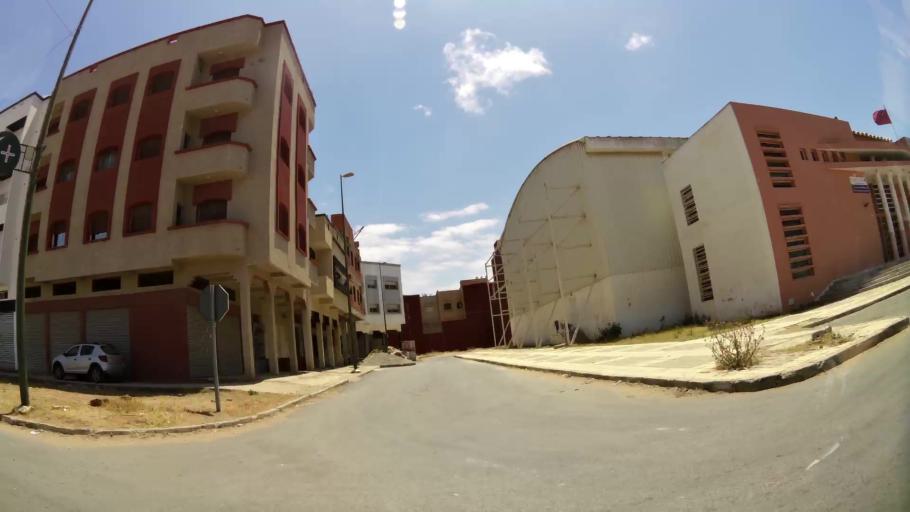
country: MA
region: Gharb-Chrarda-Beni Hssen
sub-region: Kenitra Province
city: Kenitra
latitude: 34.2346
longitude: -6.6078
